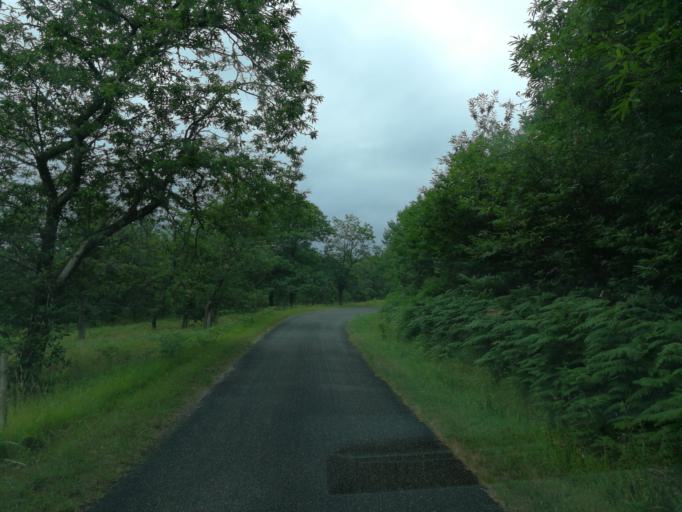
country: FR
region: Aquitaine
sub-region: Departement du Lot-et-Garonne
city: Montayral
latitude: 44.5671
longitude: 1.0758
